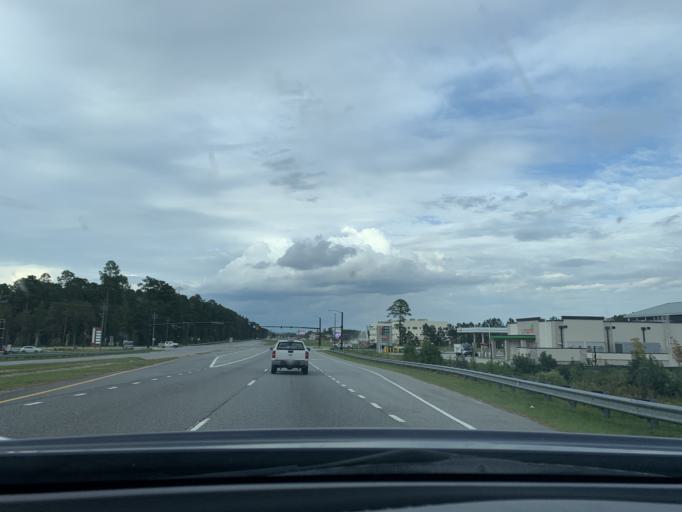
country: US
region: Georgia
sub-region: Chatham County
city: Pooler
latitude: 32.0869
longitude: -81.2780
